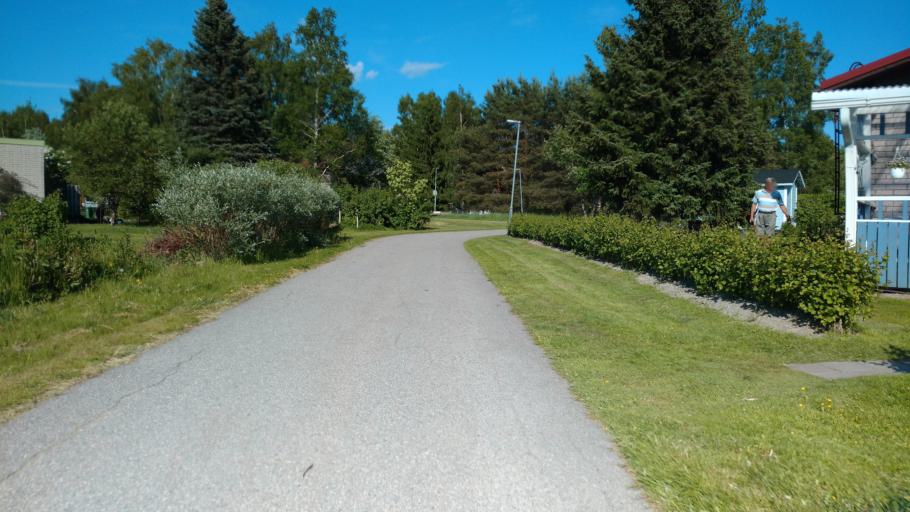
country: FI
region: Varsinais-Suomi
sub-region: Salo
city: Salo
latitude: 60.3927
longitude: 23.1592
